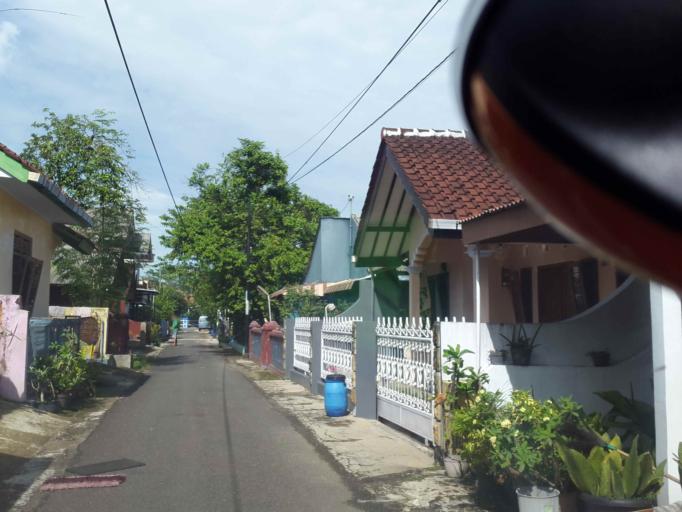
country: ID
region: Central Java
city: Wonosobo
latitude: -7.3892
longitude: 109.7253
